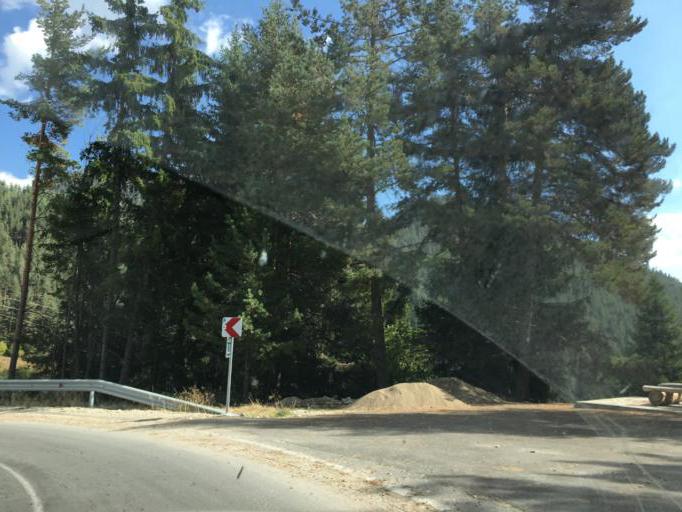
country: BG
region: Pazardzhik
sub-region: Obshtina Batak
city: Batak
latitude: 41.8891
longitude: 24.3283
